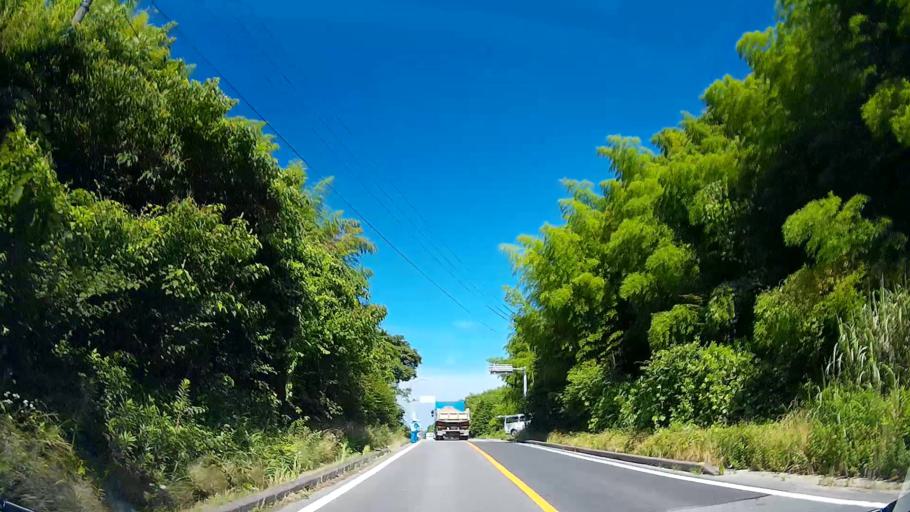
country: JP
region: Aichi
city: Gamagori
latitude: 34.8289
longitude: 137.1436
